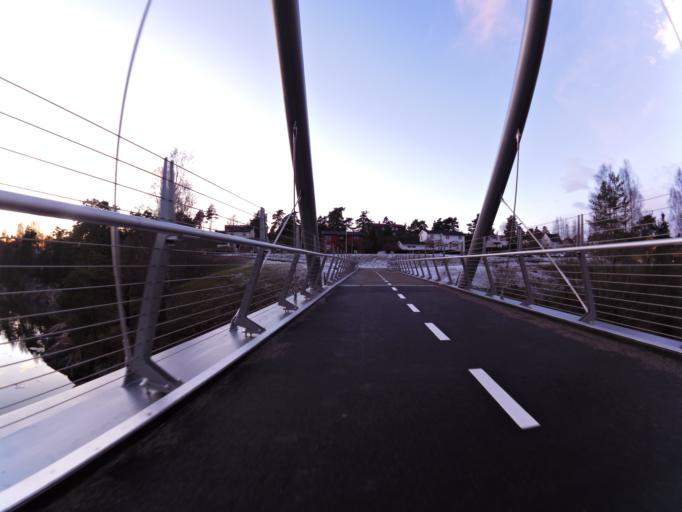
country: NO
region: Ostfold
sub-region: Sarpsborg
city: Sarpsborg
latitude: 59.2909
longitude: 11.1364
